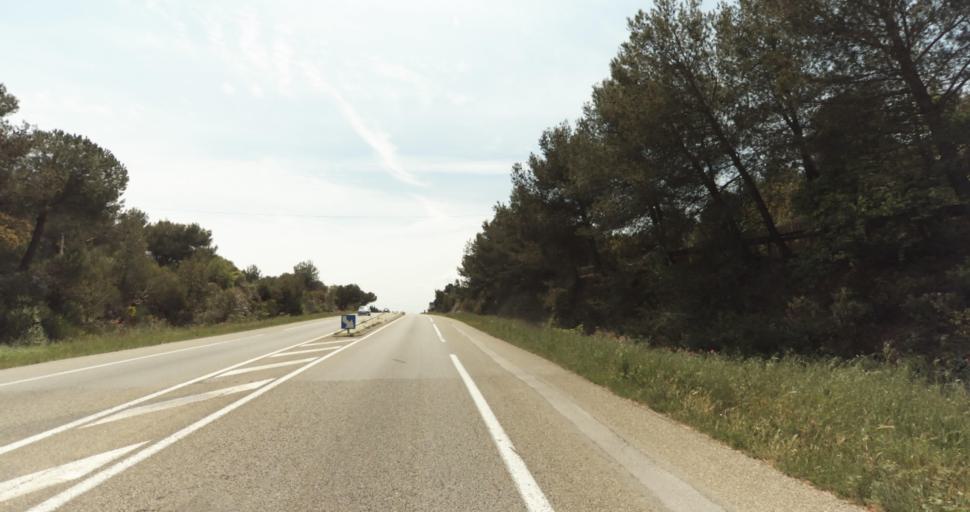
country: FR
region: Languedoc-Roussillon
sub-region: Departement du Gard
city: Nimes
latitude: 43.8615
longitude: 4.3235
